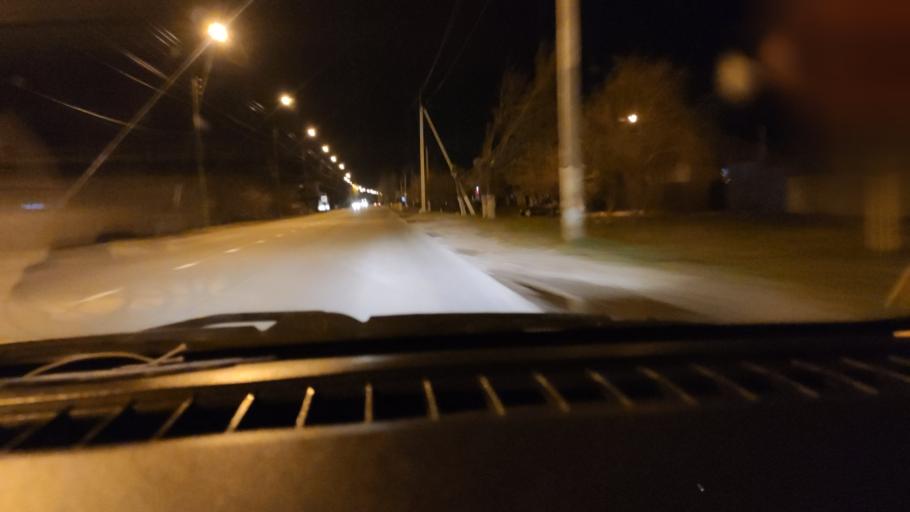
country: RU
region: Saratov
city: Privolzhskiy
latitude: 51.4312
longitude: 46.0552
